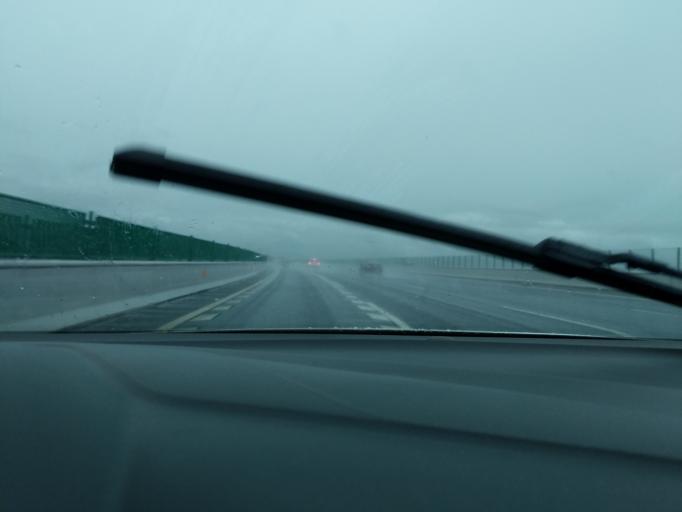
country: CN
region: Guangdong
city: Zhishan
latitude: 22.4869
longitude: 112.7967
